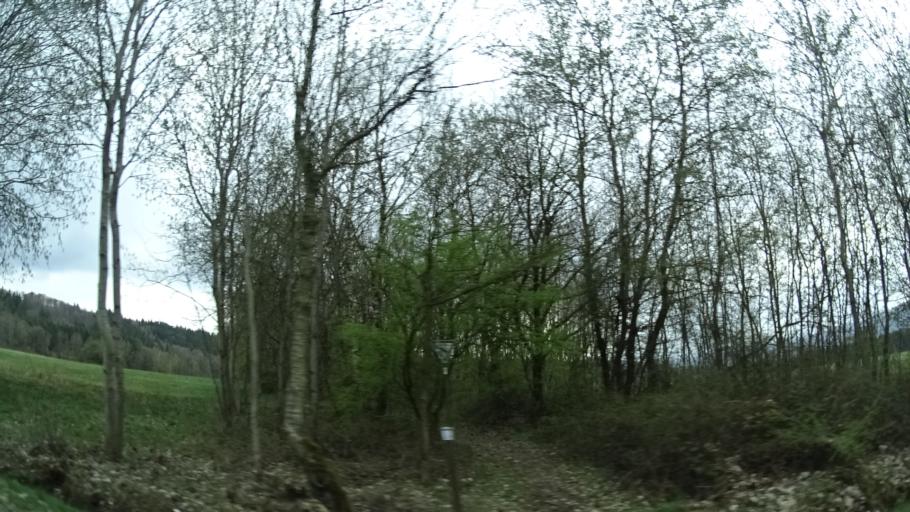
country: DE
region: Rheinland-Pfalz
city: Weitersborn
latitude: 49.8756
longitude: 7.5299
